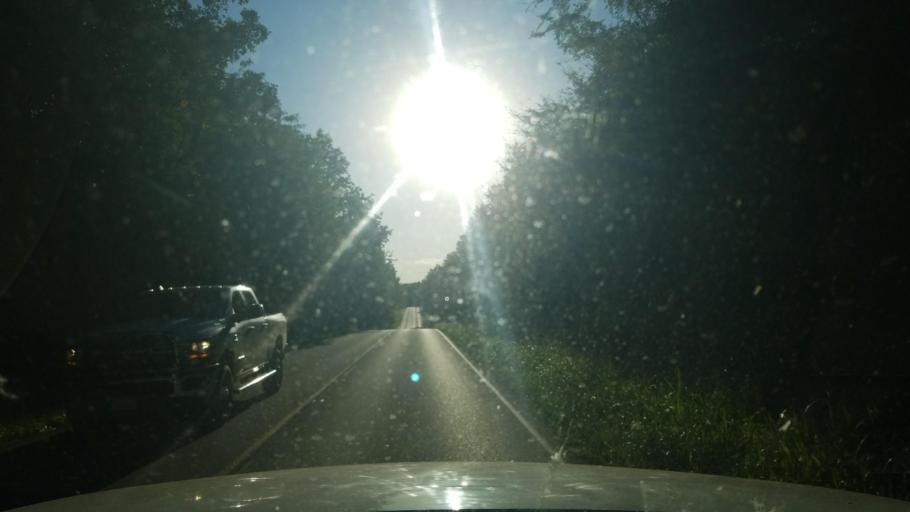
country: US
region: Illinois
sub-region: Hardin County
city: Elizabethtown
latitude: 37.5776
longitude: -88.3788
